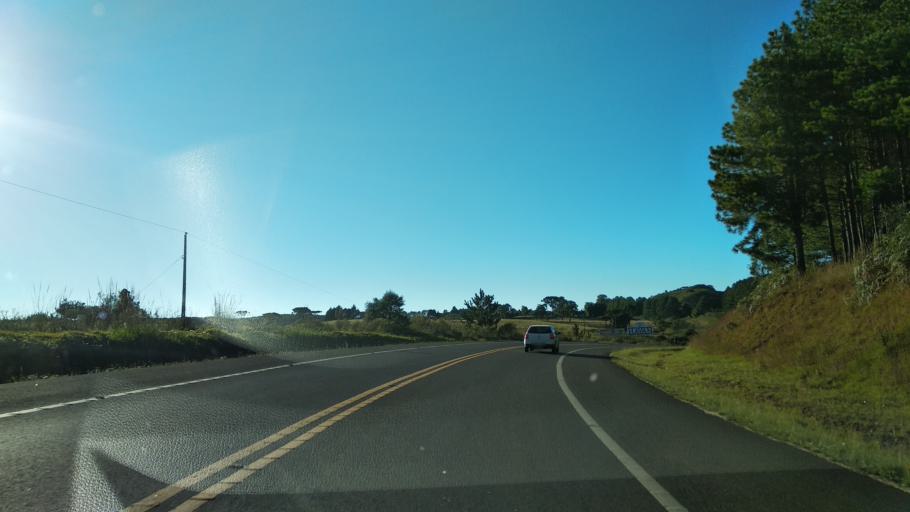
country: BR
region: Santa Catarina
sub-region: Lages
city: Lages
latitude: -27.7875
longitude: -50.4254
